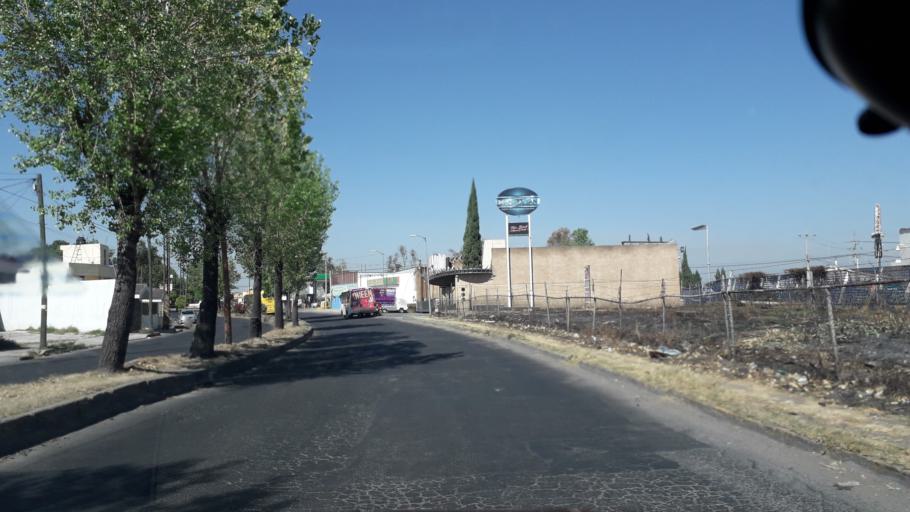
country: MX
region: Puebla
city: Puebla
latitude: 19.0804
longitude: -98.2151
